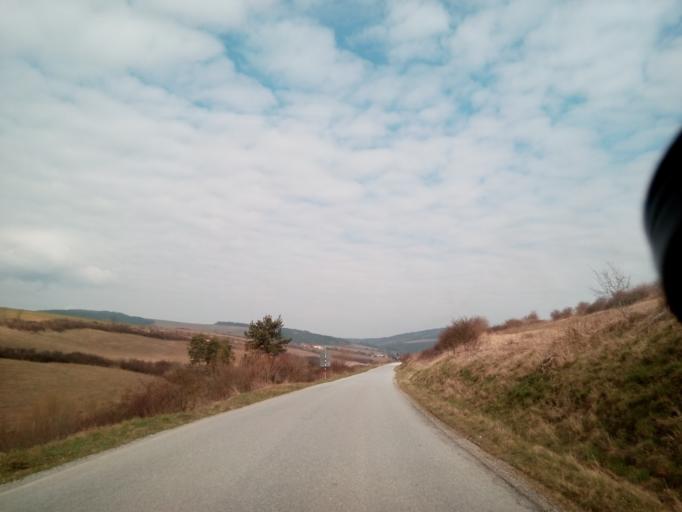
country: SK
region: Presovsky
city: Sabinov
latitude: 49.0297
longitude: 21.0193
